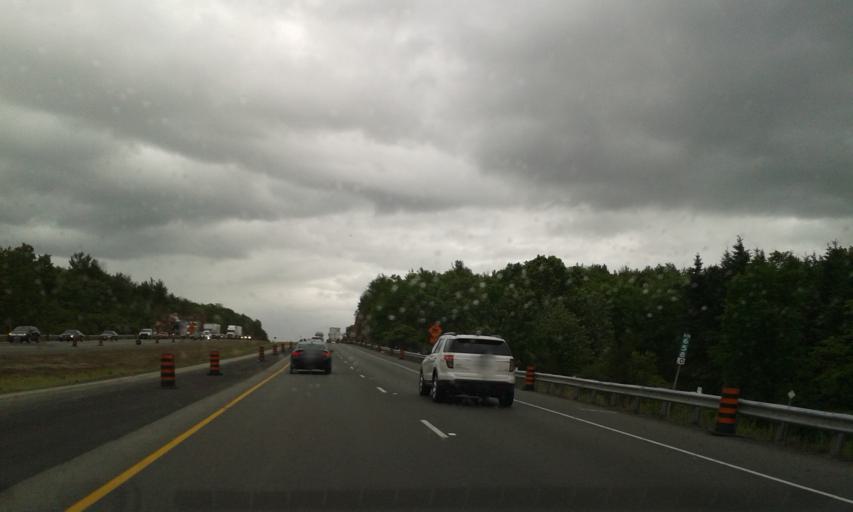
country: US
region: New York
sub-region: Jefferson County
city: Alexandria Bay
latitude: 44.3784
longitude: -76.0218
